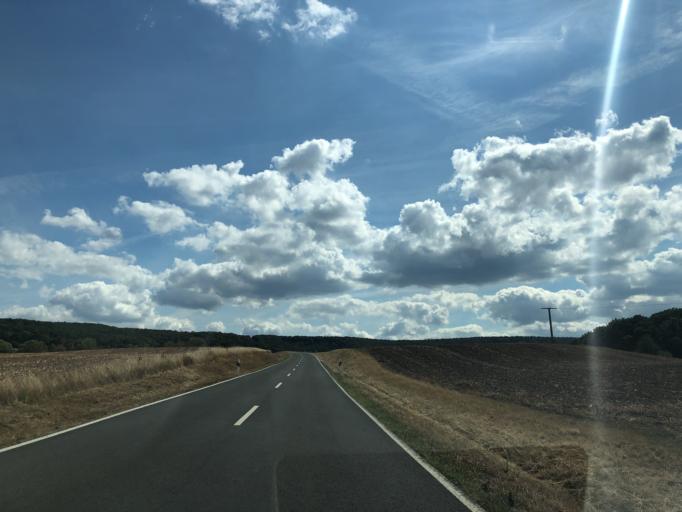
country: DE
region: Bavaria
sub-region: Regierungsbezirk Unterfranken
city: Oberschwarzach
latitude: 49.8383
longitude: 10.4341
